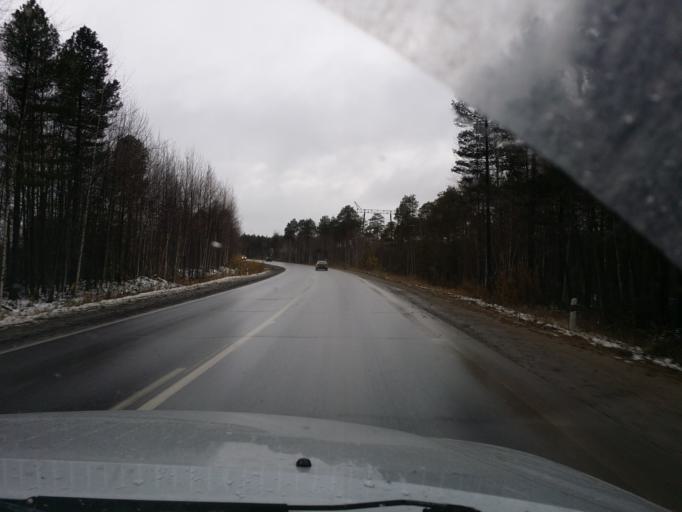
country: RU
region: Khanty-Mansiyskiy Avtonomnyy Okrug
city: Megion
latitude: 61.1633
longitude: 75.6935
